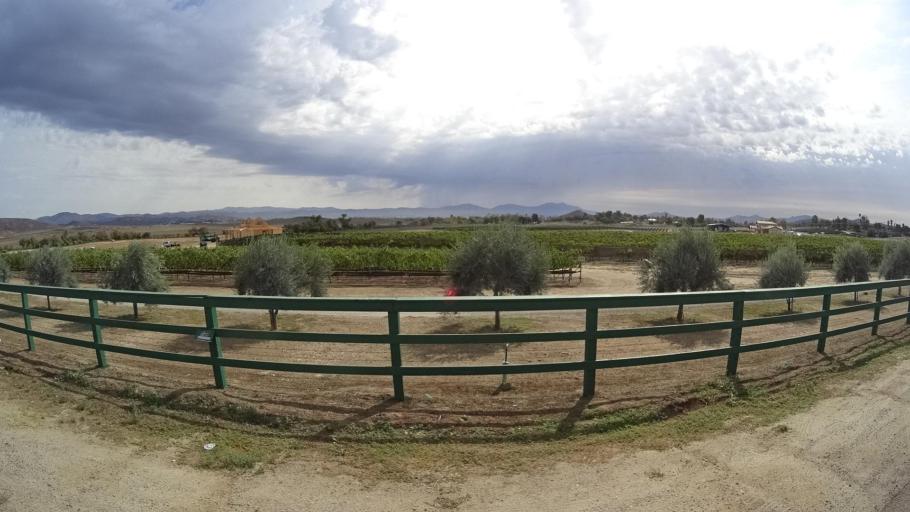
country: US
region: California
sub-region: San Diego County
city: San Pasqual
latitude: 33.0290
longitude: -116.9361
